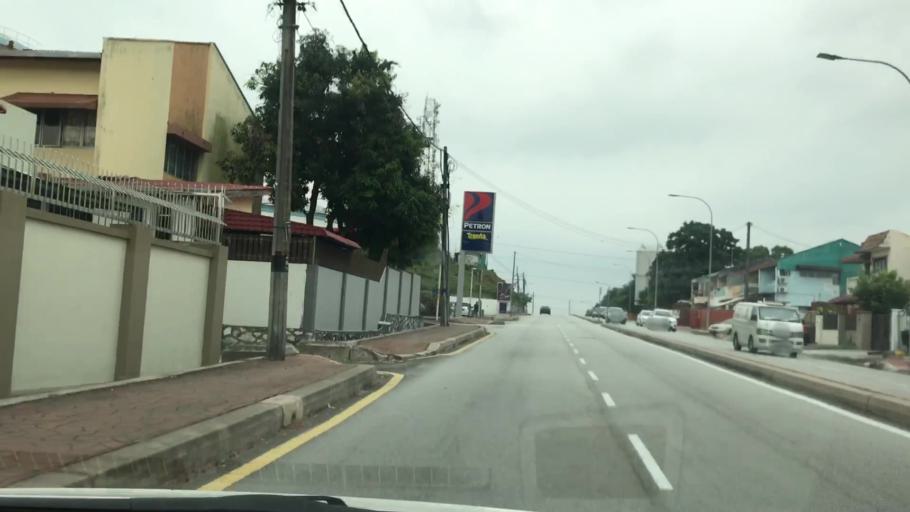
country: MY
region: Selangor
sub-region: Petaling
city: Petaling Jaya
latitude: 3.1123
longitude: 101.6195
